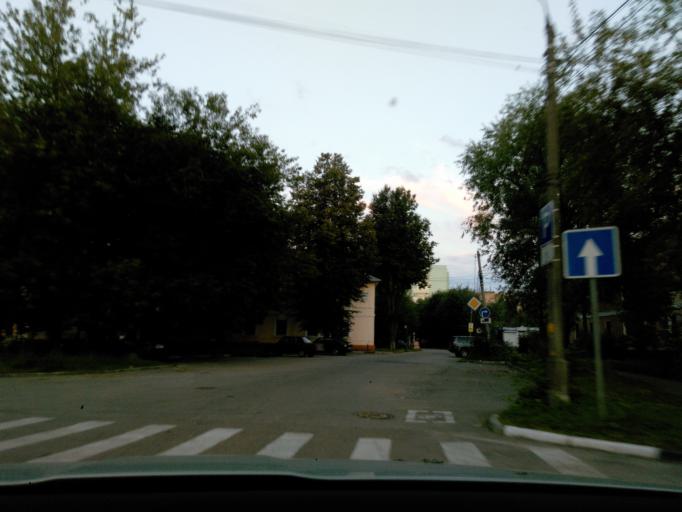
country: RU
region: Moskovskaya
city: Klin
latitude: 56.3375
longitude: 36.7220
